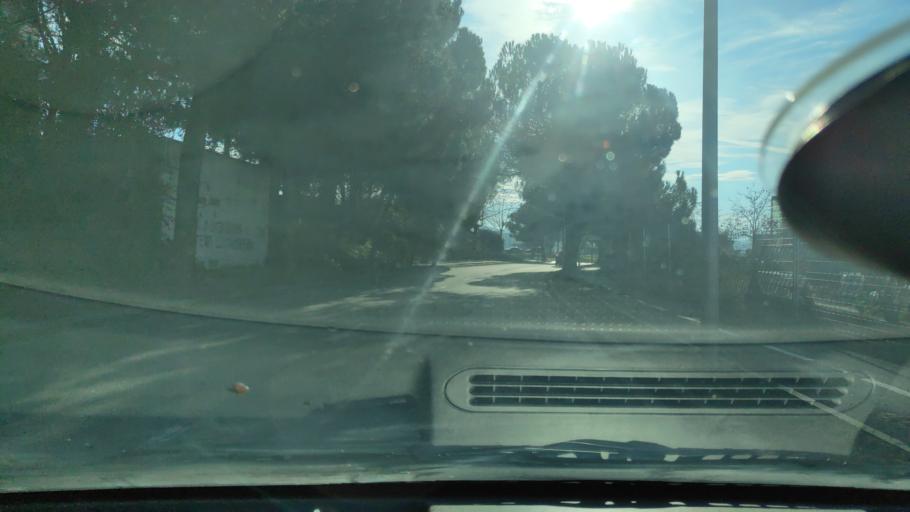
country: ES
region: Catalonia
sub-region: Provincia de Barcelona
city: Rubi
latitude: 41.4883
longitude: 2.0516
